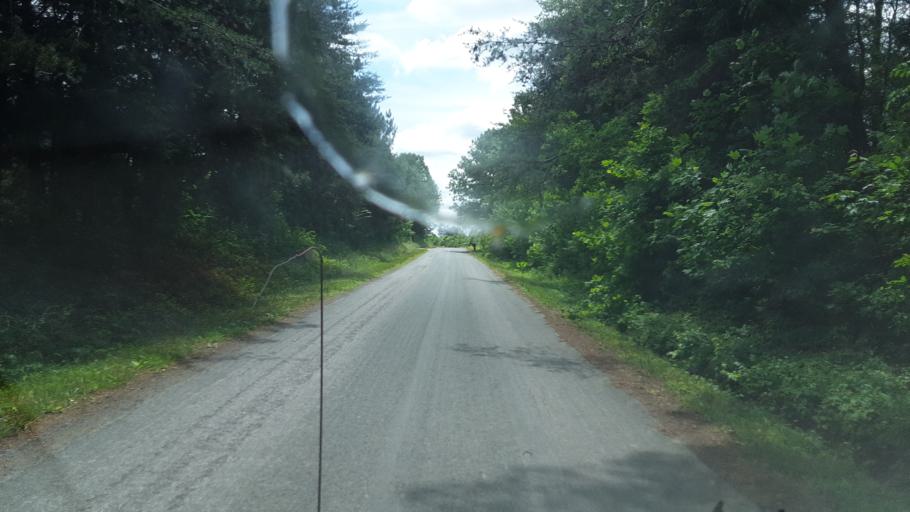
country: US
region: Virginia
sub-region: Pittsylvania County
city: Chatham
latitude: 36.8481
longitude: -79.4264
